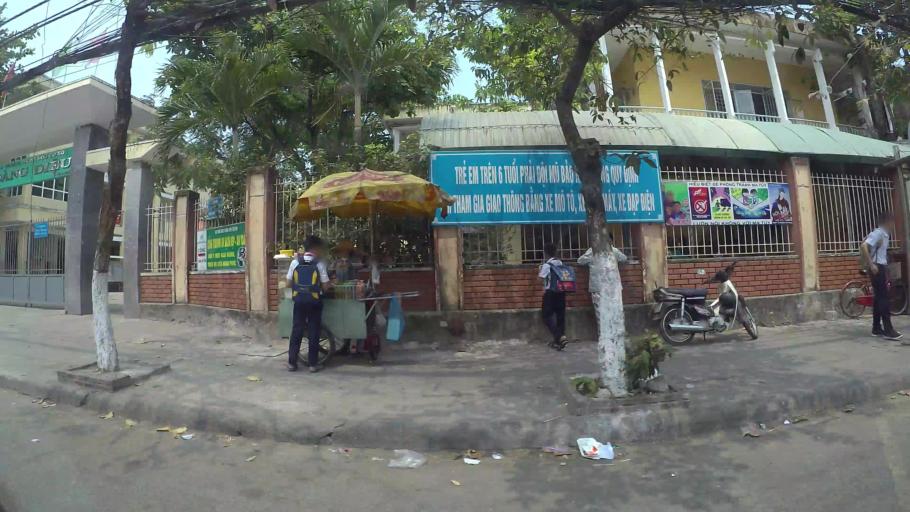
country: VN
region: Da Nang
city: Da Nang
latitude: 16.0725
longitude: 108.2082
